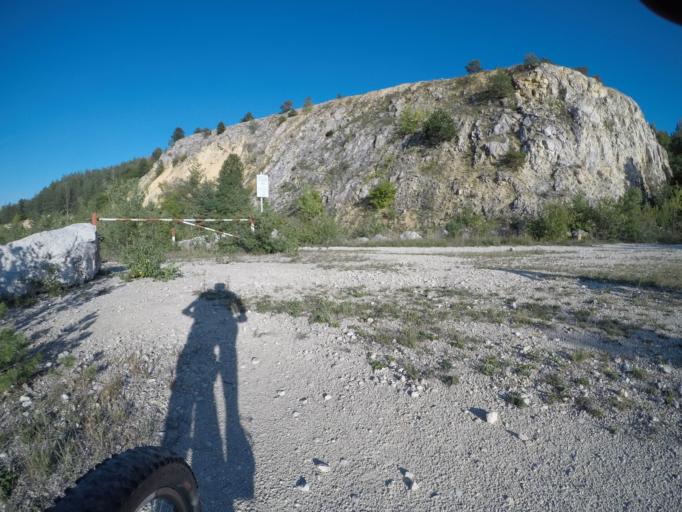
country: AT
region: Lower Austria
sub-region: Politischer Bezirk Bruck an der Leitha
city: Mannersdorf am Leithagebirge
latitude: 47.9672
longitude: 16.6128
